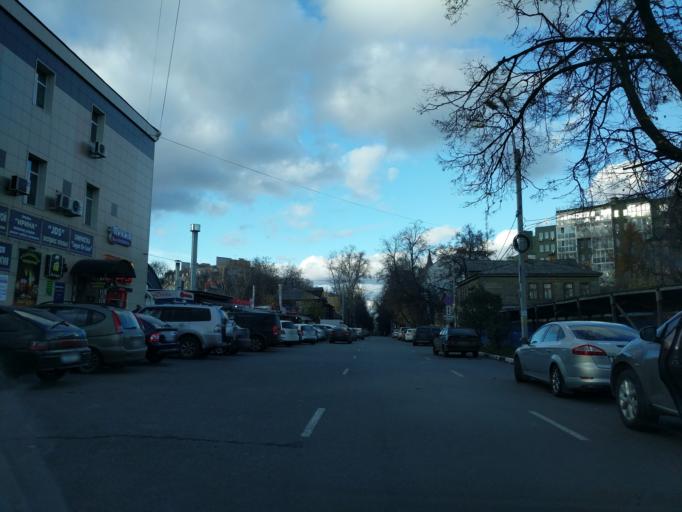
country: RU
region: Nizjnij Novgorod
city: Nizhniy Novgorod
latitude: 56.3092
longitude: 43.9914
